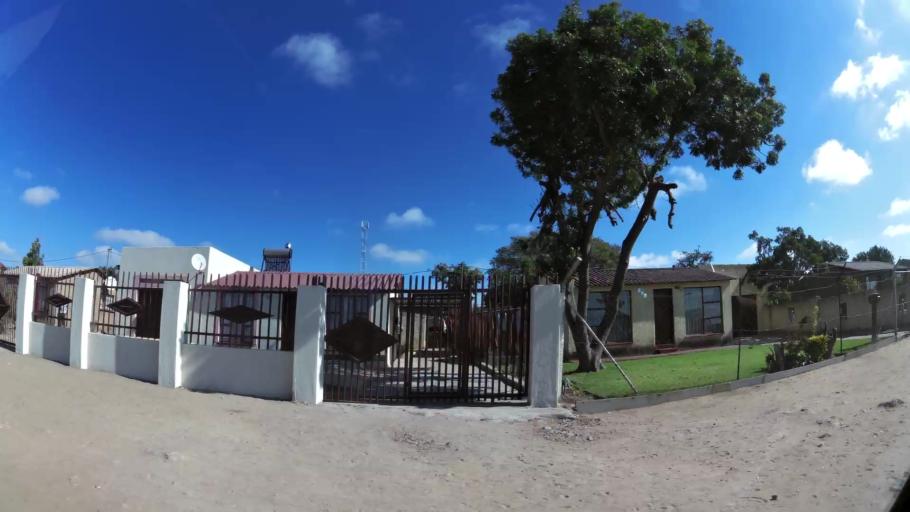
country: ZA
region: Limpopo
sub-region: Capricorn District Municipality
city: Polokwane
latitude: -23.8637
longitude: 29.3913
